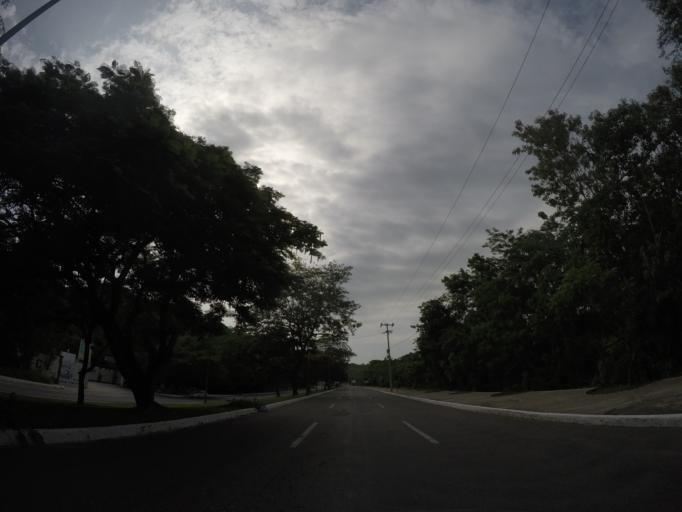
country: MX
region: Oaxaca
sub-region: Santa Maria Huatulco
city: Sector H Tres
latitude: 15.7800
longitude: -96.1537
